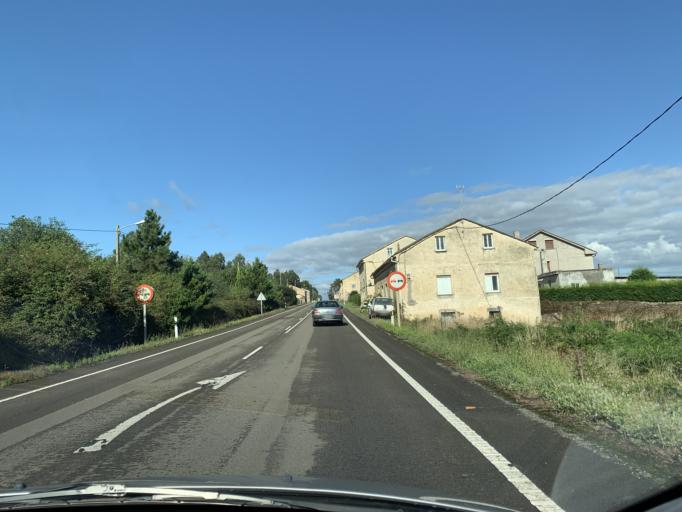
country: ES
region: Galicia
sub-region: Provincia de Lugo
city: Barreiros
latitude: 43.5449
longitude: -7.2122
